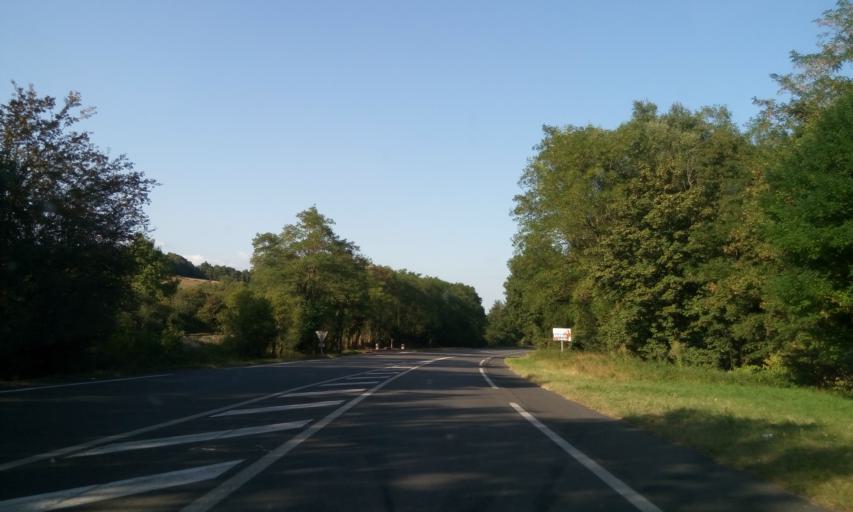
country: FR
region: Rhone-Alpes
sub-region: Departement du Rhone
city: Lissieu
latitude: 45.8530
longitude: 4.7343
